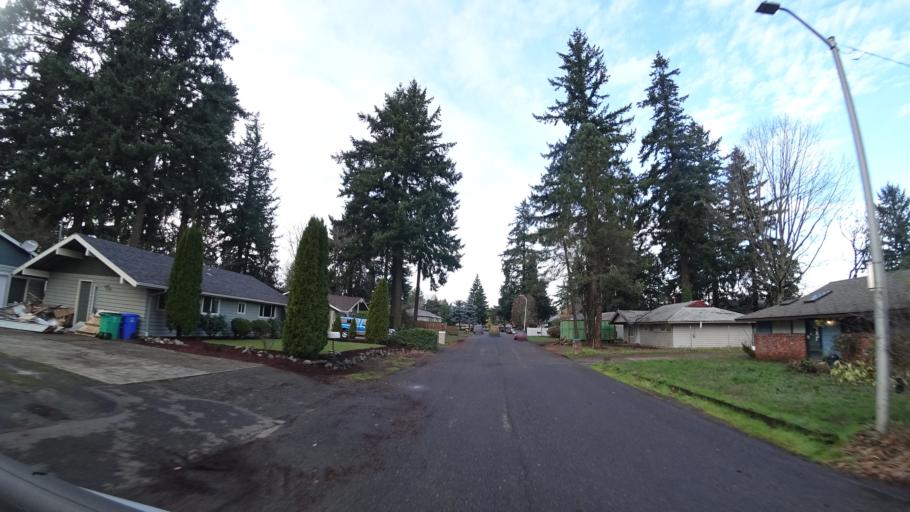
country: US
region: Oregon
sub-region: Multnomah County
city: Lents
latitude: 45.5181
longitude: -122.5228
